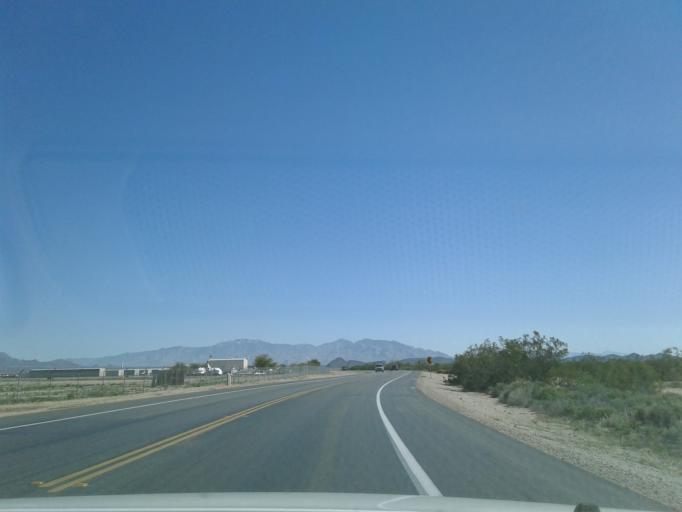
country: US
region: Arizona
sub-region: Pima County
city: Marana
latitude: 32.4027
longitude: -111.2253
